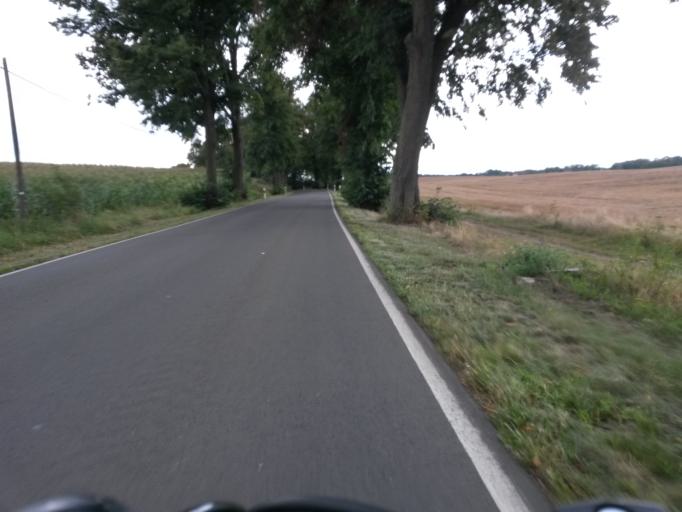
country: DE
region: Brandenburg
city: Angermunde
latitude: 53.0102
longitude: 13.9600
